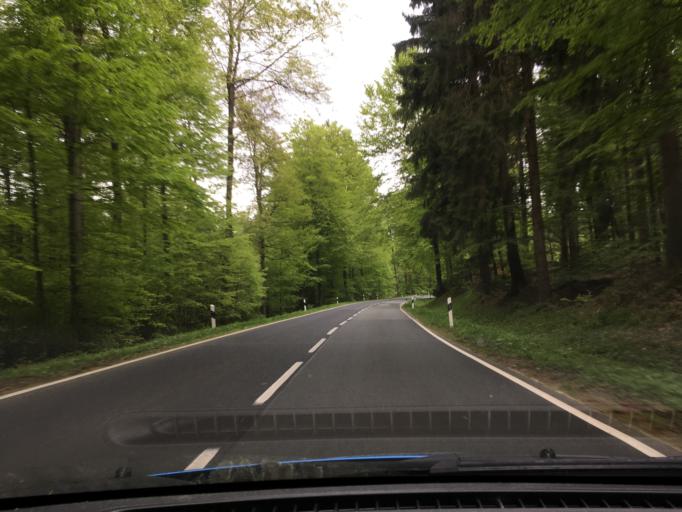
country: DE
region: Lower Saxony
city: Derental
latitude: 51.6859
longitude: 9.4523
